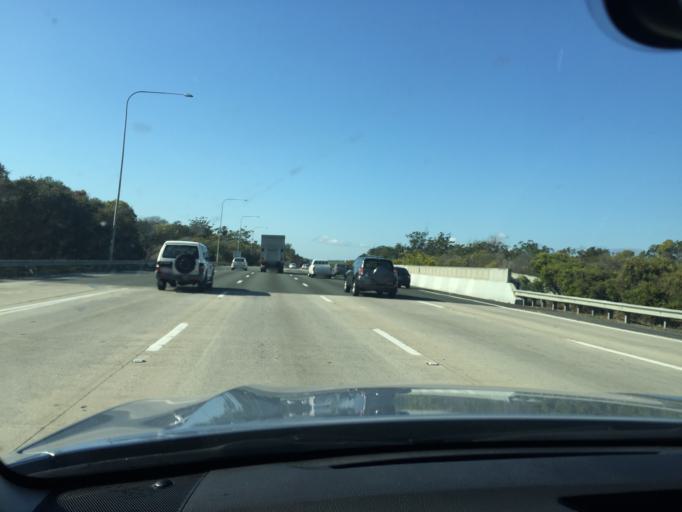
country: AU
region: Queensland
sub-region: Gold Coast
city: Yatala
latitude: -27.7391
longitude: 153.2309
